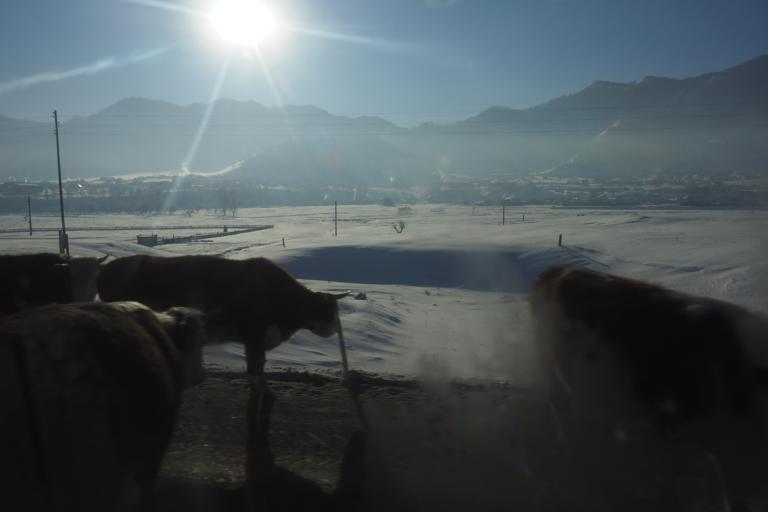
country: RU
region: Altay
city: Onguday
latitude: 50.7450
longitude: 86.1572
